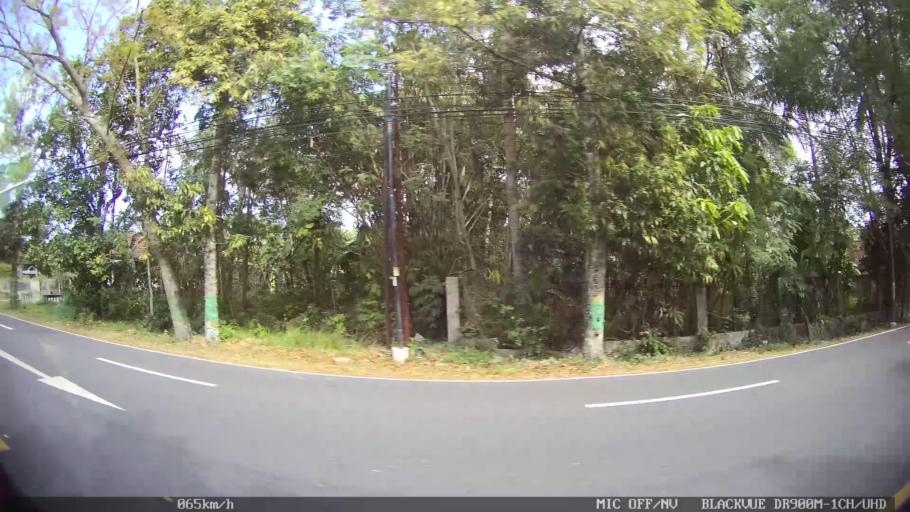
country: ID
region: Daerah Istimewa Yogyakarta
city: Srandakan
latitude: -7.8867
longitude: 110.1305
